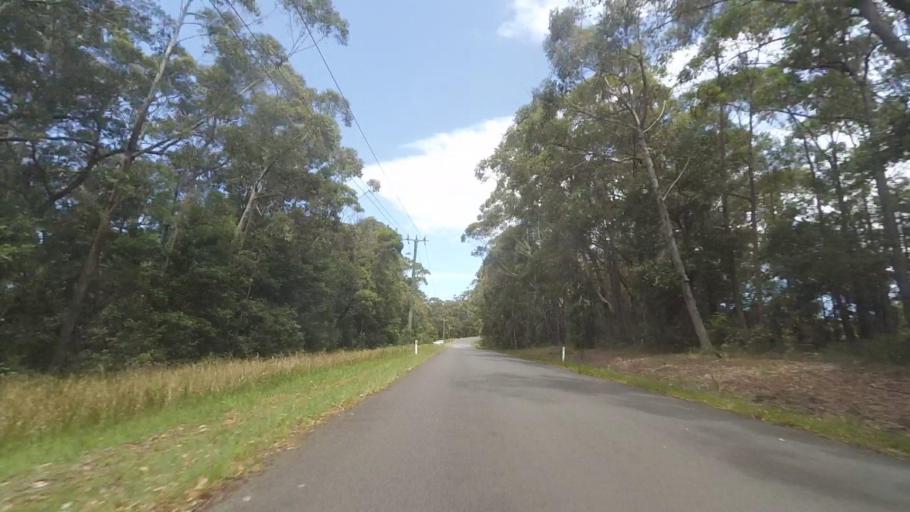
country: AU
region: New South Wales
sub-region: Shoalhaven Shire
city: Milton
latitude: -35.3908
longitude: 150.3674
